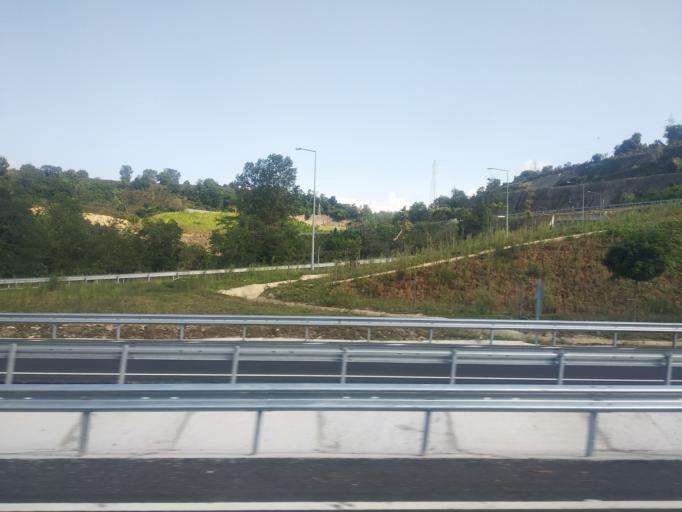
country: TR
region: Ordu
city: Ordu
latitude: 40.9902
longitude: 37.8136
